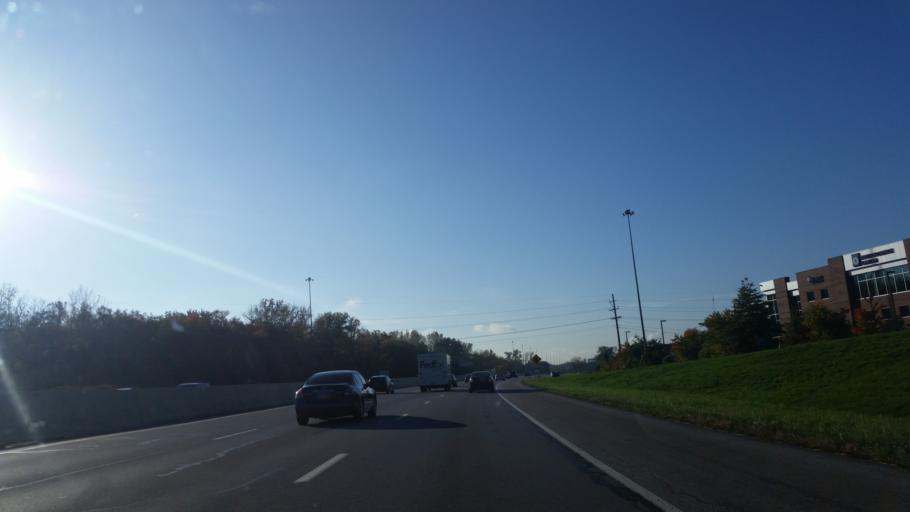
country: US
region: Ohio
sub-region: Summit County
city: Fairlawn
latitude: 41.0985
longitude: -81.5873
